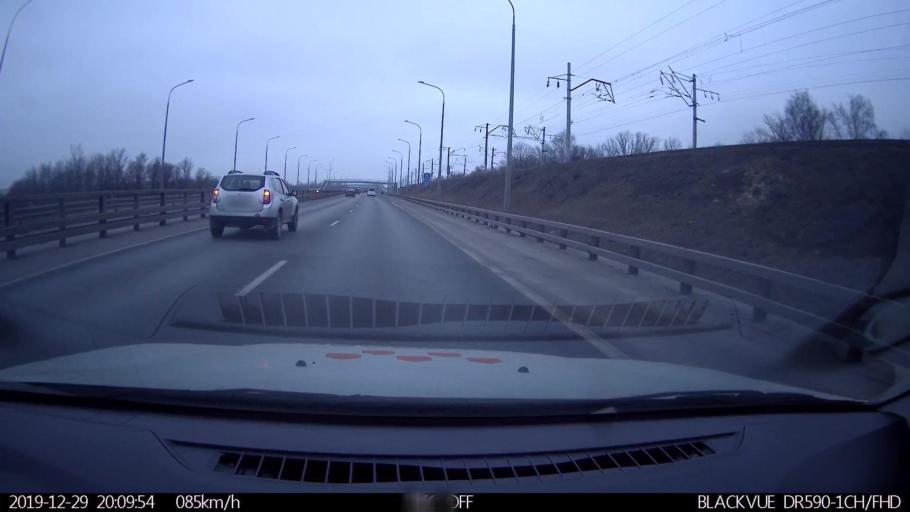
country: RU
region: Nizjnij Novgorod
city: Neklyudovo
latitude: 56.3706
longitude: 43.9441
